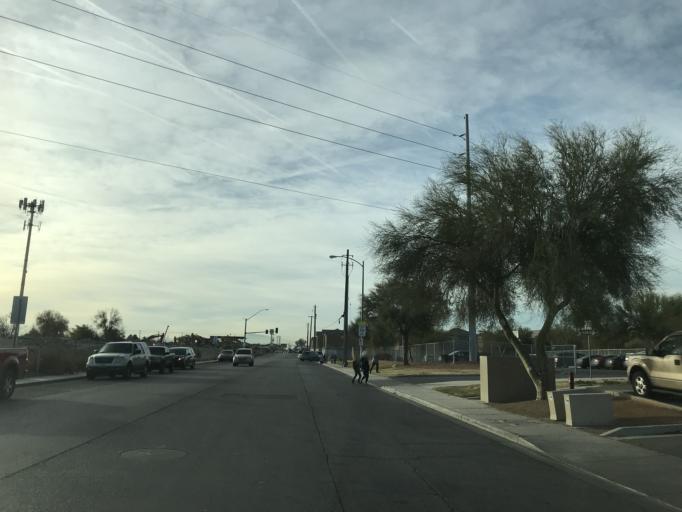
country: US
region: Nevada
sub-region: Clark County
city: Nellis Air Force Base
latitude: 36.2376
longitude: -115.0667
